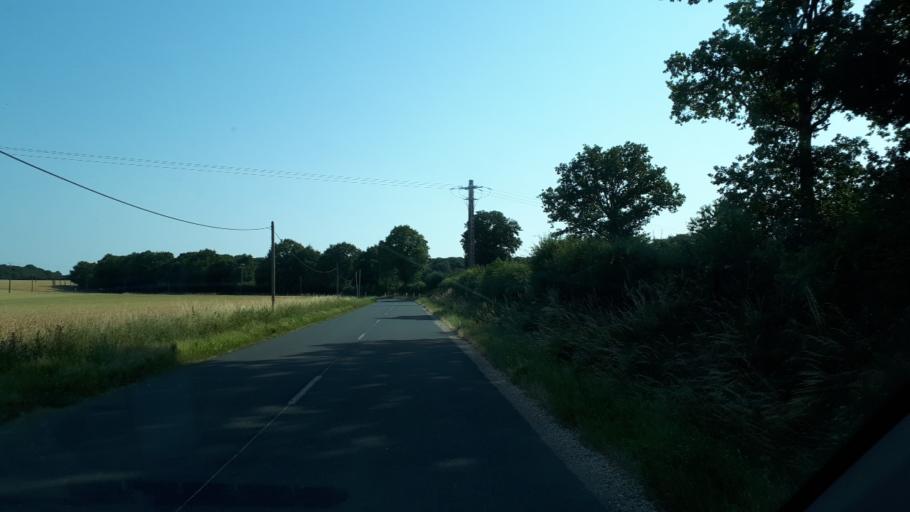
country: FR
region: Centre
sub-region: Departement du Loir-et-Cher
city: Droue
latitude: 48.0279
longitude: 1.0640
